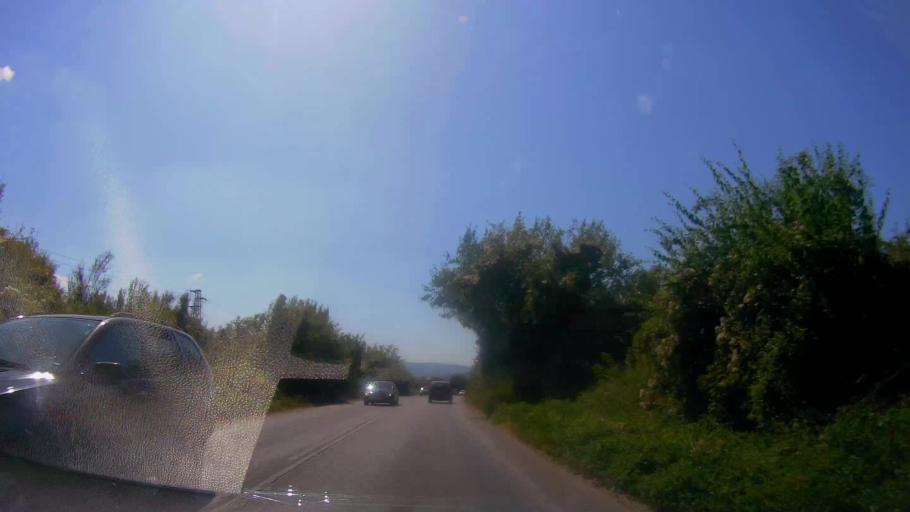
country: BG
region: Veliko Turnovo
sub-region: Obshtina Gorna Oryakhovitsa
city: Purvomaytsi
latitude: 43.2314
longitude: 25.6402
